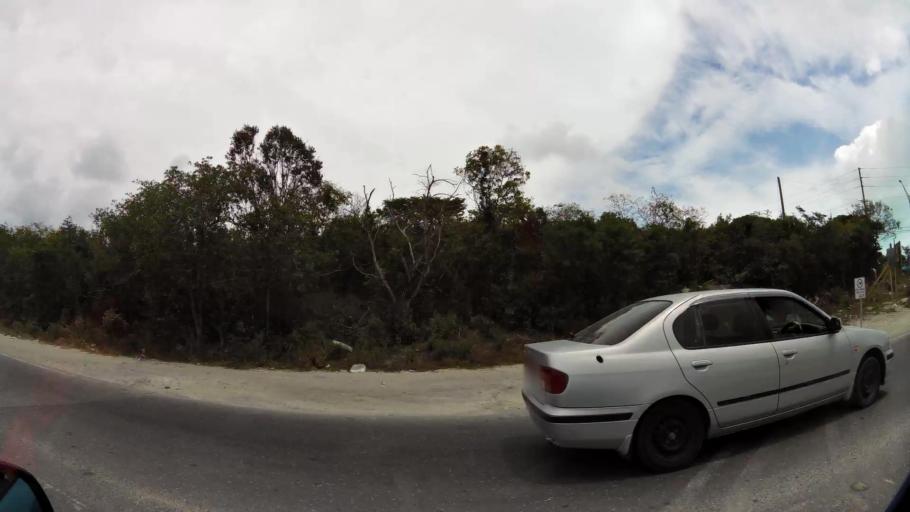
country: BS
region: Mayaguana
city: Abraham's Bay
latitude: 21.7809
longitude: -72.2558
